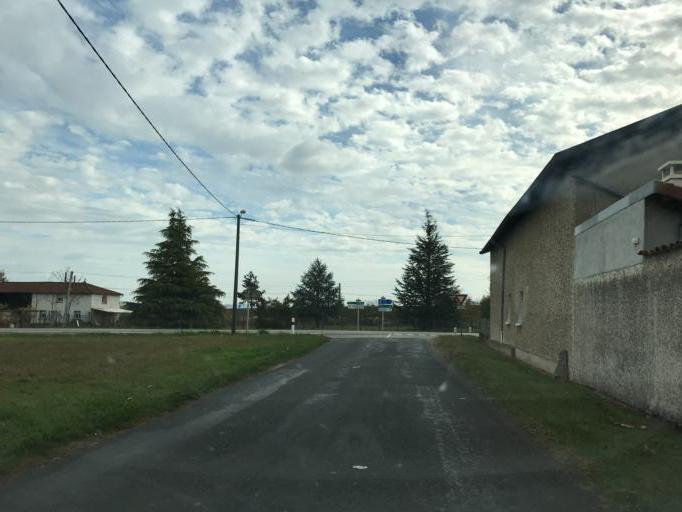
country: FR
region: Rhone-Alpes
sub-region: Departement de l'Ain
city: Beligneux
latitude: 45.8660
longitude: 5.1471
